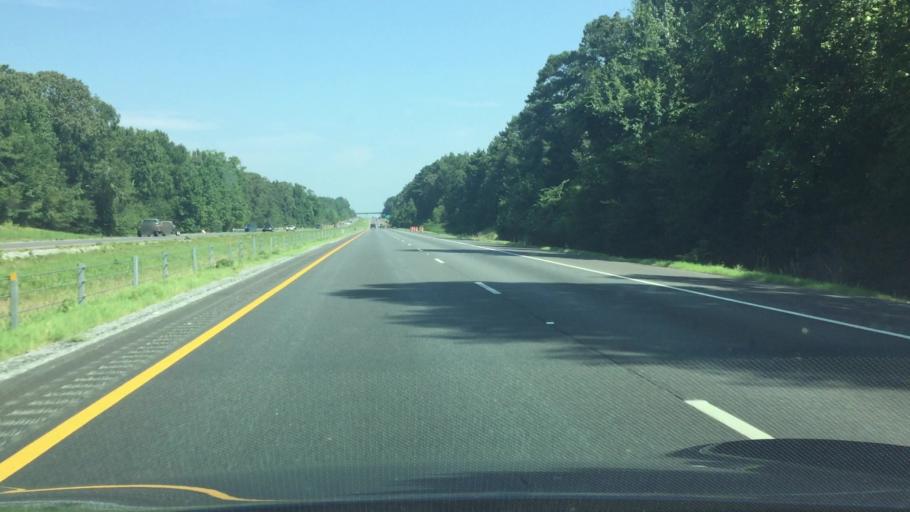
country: US
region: Alabama
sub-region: Chilton County
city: Clanton
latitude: 32.8205
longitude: -86.5869
